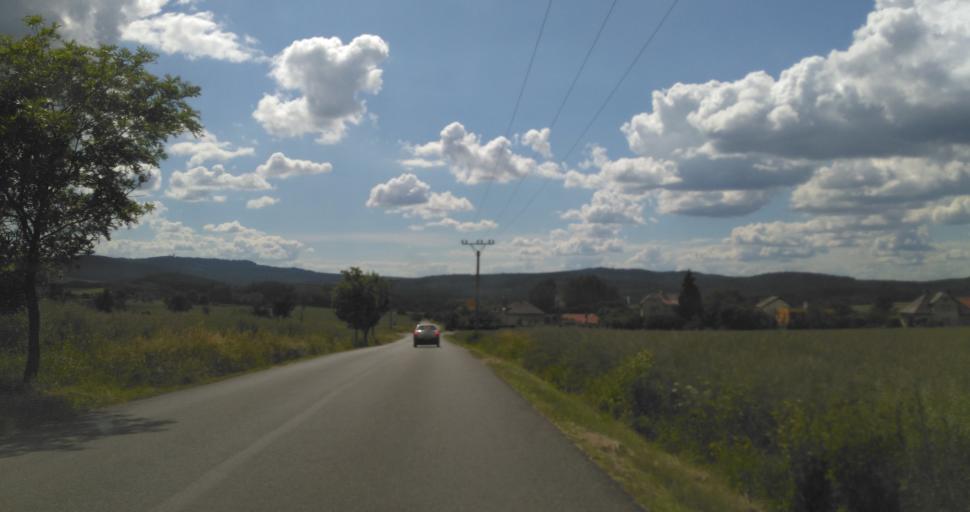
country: CZ
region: Plzensky
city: Zbiroh
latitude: 49.8531
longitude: 13.7551
